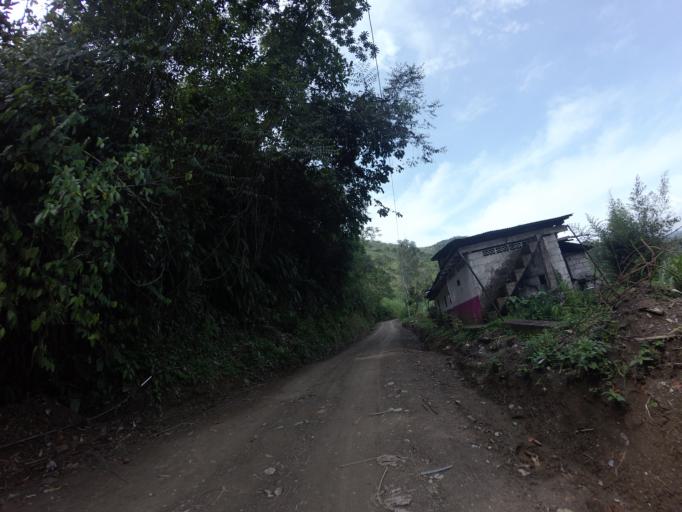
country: CO
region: Caldas
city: Marquetalia
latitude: 5.3286
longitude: -75.0484
